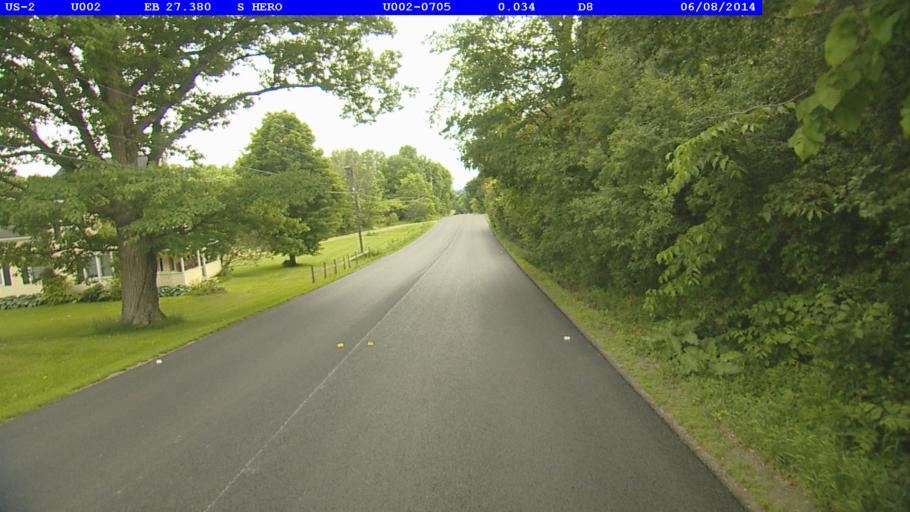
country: US
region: New York
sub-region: Clinton County
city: Cumberland Head
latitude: 44.6797
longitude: -73.3162
